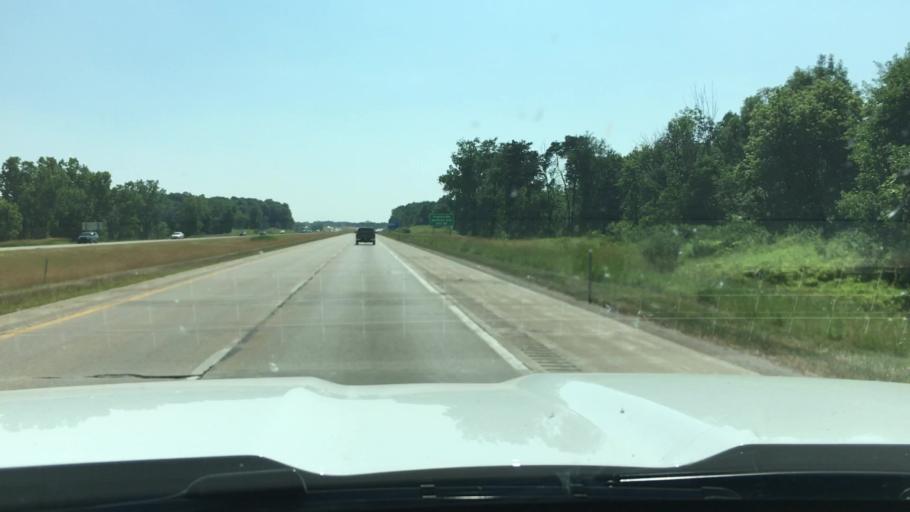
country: US
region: Michigan
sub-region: Eaton County
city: Waverly
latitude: 42.7978
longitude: -84.6436
